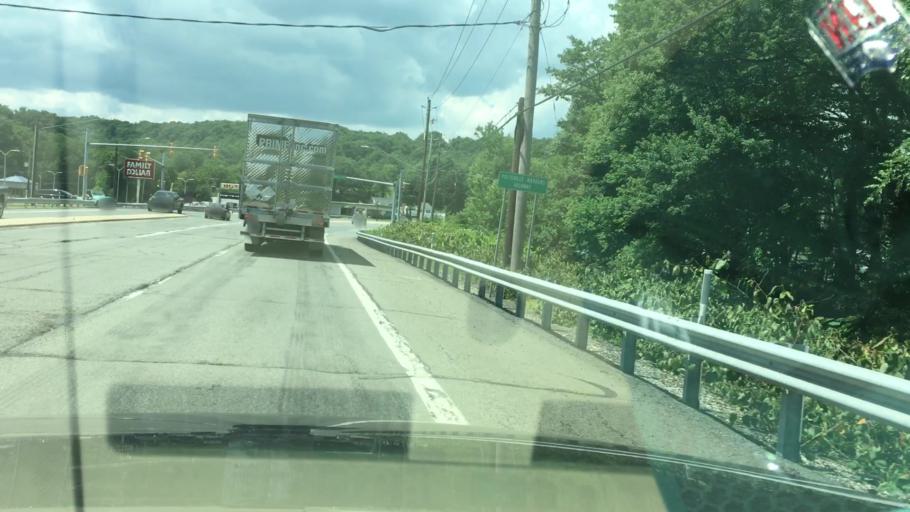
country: US
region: Pennsylvania
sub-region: Schuylkill County
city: Minersville
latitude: 40.6816
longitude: -76.2515
